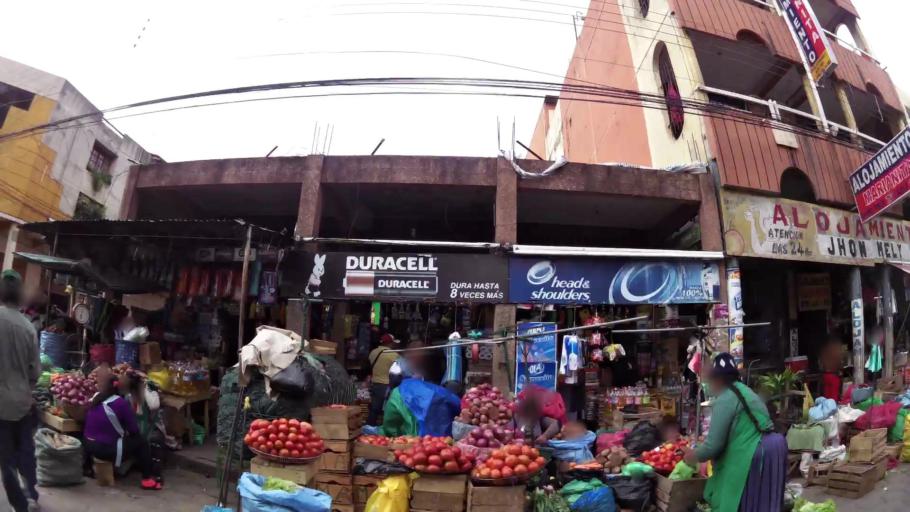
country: BO
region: Santa Cruz
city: Santa Cruz de la Sierra
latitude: -17.7780
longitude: -63.1758
